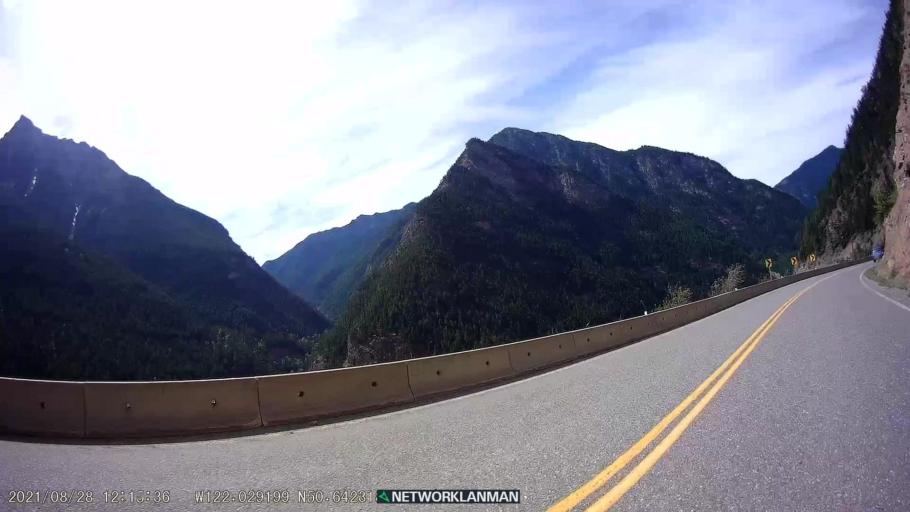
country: CA
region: British Columbia
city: Lillooet
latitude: 50.6418
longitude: -122.0305
